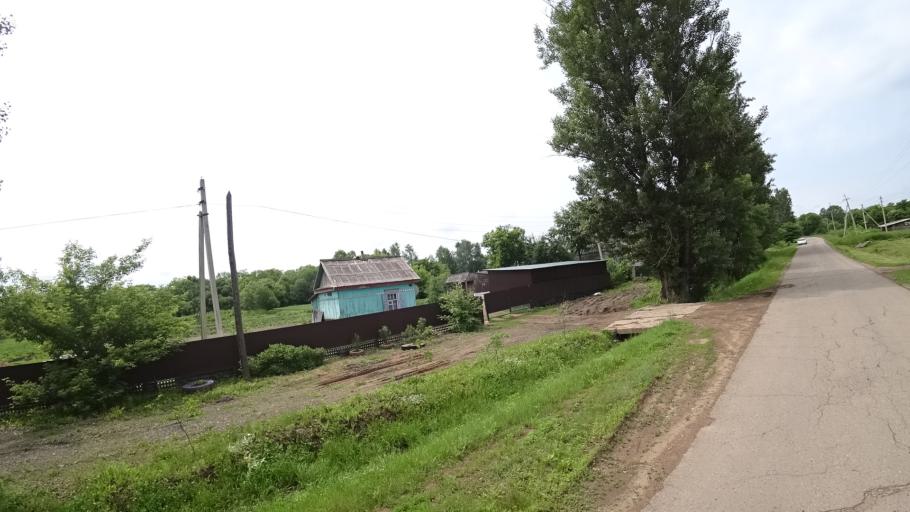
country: RU
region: Primorskiy
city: Novosysoyevka
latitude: 44.2471
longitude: 133.3740
